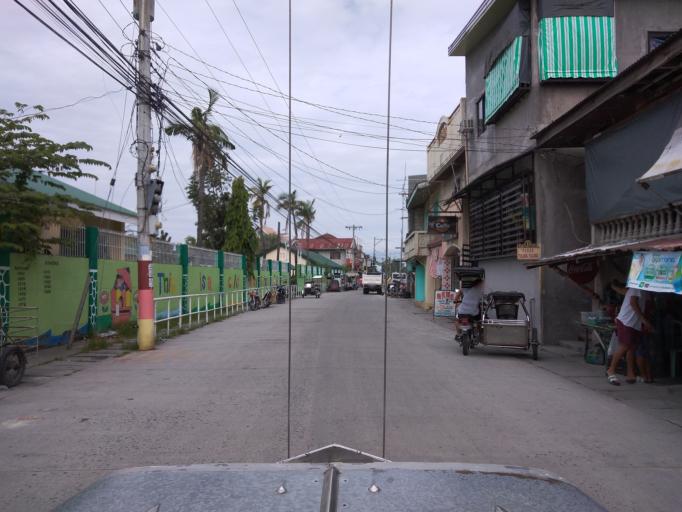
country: PH
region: Central Luzon
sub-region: Province of Pampanga
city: Sexmoan
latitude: 14.9373
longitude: 120.6219
